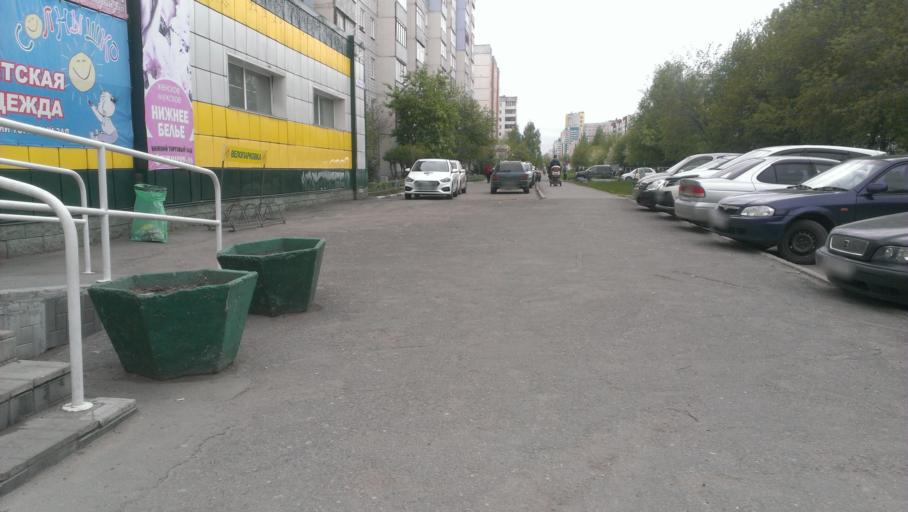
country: RU
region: Altai Krai
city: Novosilikatnyy
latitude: 53.3389
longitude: 83.6752
